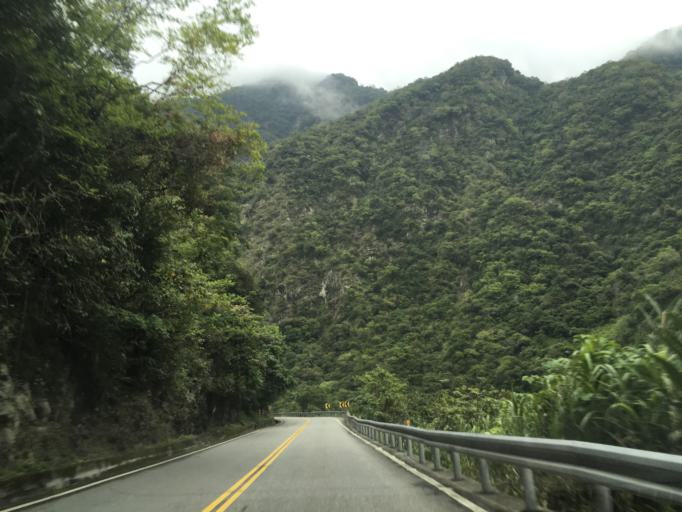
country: TW
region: Taiwan
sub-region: Hualien
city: Hualian
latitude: 24.1745
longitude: 121.5873
